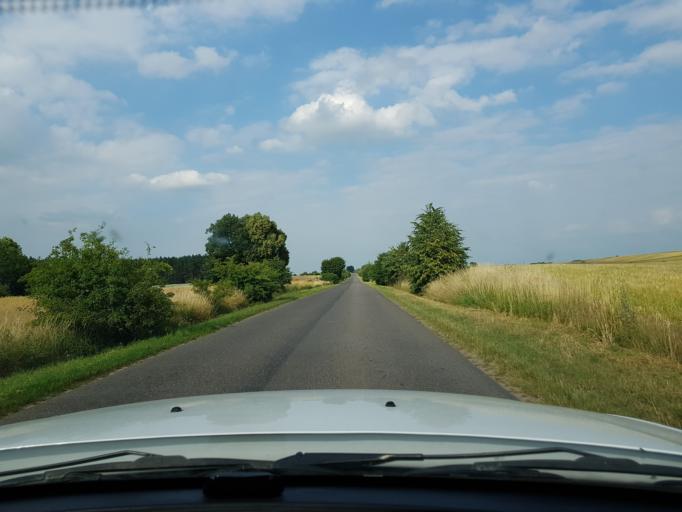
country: PL
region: West Pomeranian Voivodeship
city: Trzcinsko Zdroj
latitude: 53.0098
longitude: 14.5303
